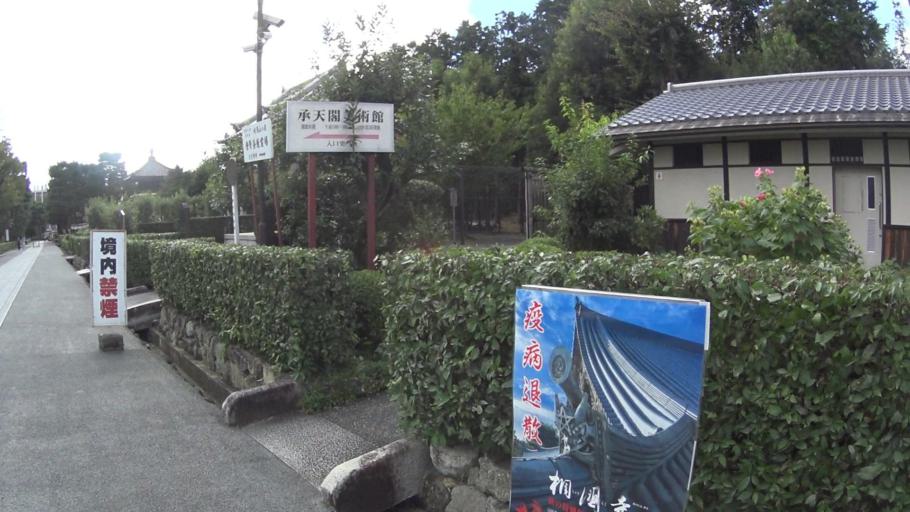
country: JP
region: Kyoto
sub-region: Kyoto-shi
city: Kamigyo-ku
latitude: 35.0329
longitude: 135.7616
